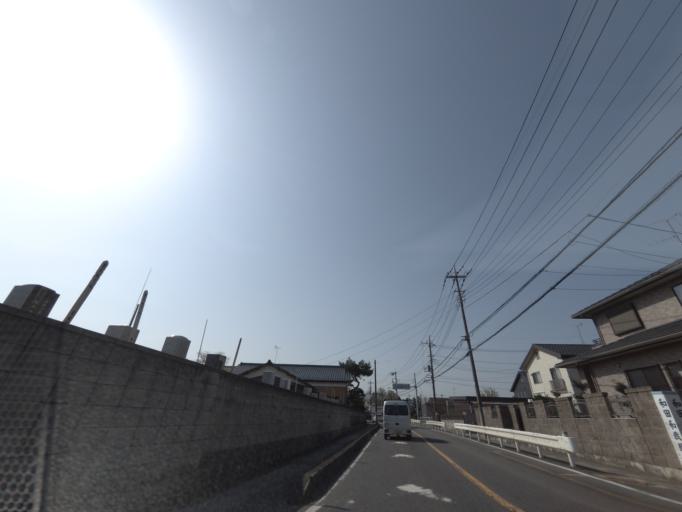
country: JP
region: Saitama
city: Yono
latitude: 35.8772
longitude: 139.5974
